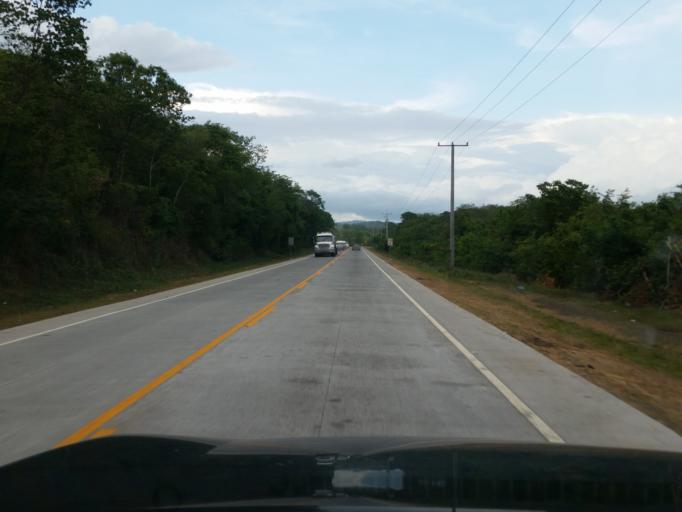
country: NI
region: Managua
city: Carlos Fonseca Amador
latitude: 12.0625
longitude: -86.4551
